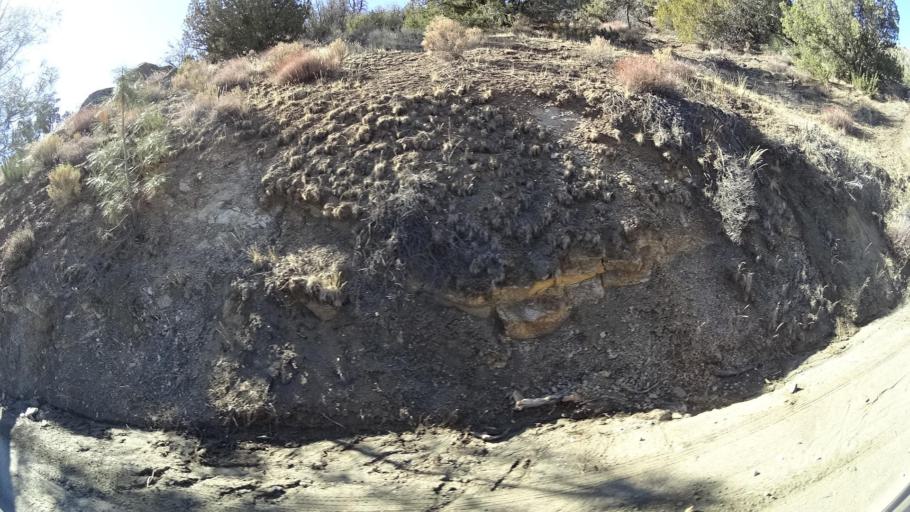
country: US
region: California
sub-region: Kern County
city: Wofford Heights
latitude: 35.7036
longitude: -118.4789
